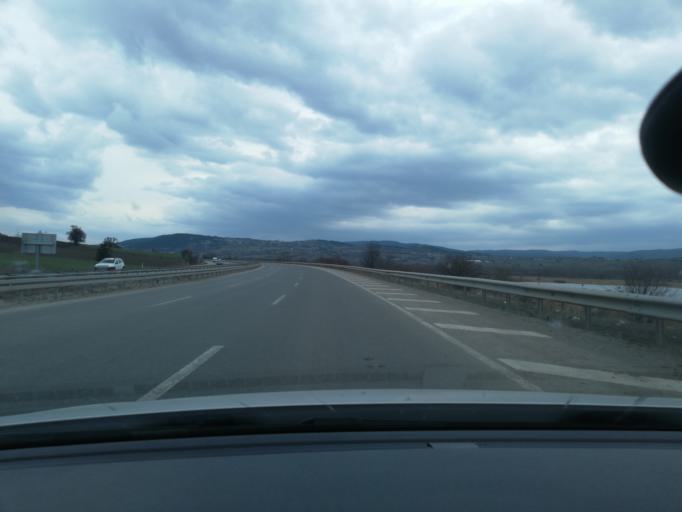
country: TR
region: Bolu
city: Yenicaga
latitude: 40.7733
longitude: 32.0164
